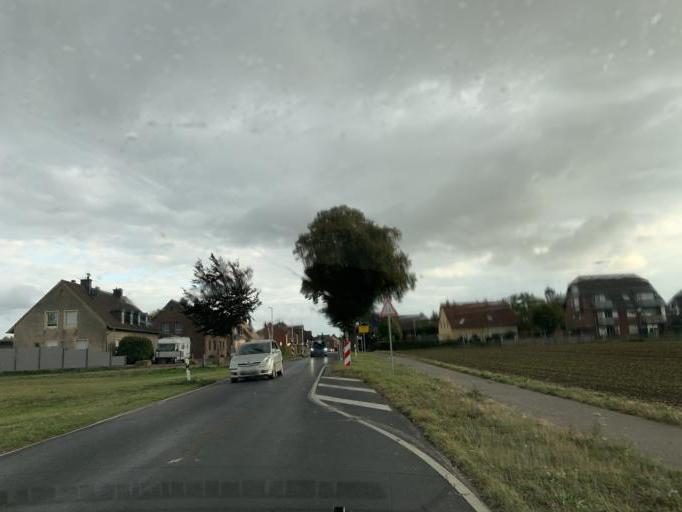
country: DE
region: North Rhine-Westphalia
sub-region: Regierungsbezirk Koln
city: Linnich
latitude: 50.9676
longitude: 6.2729
